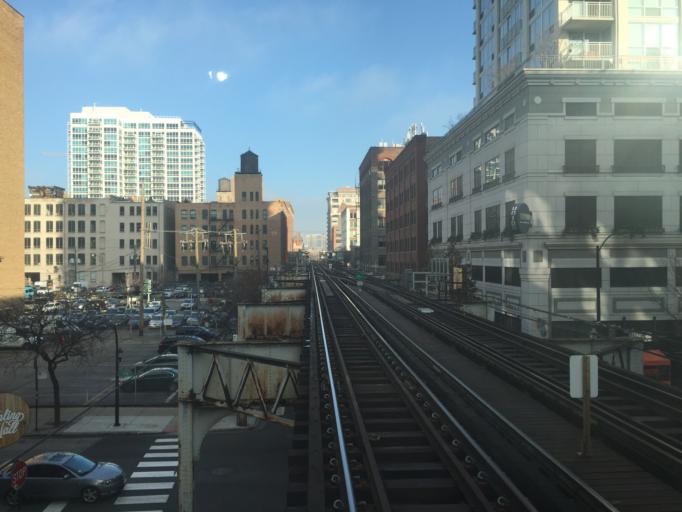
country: US
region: Illinois
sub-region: Cook County
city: Chicago
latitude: 41.8939
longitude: -87.6357
